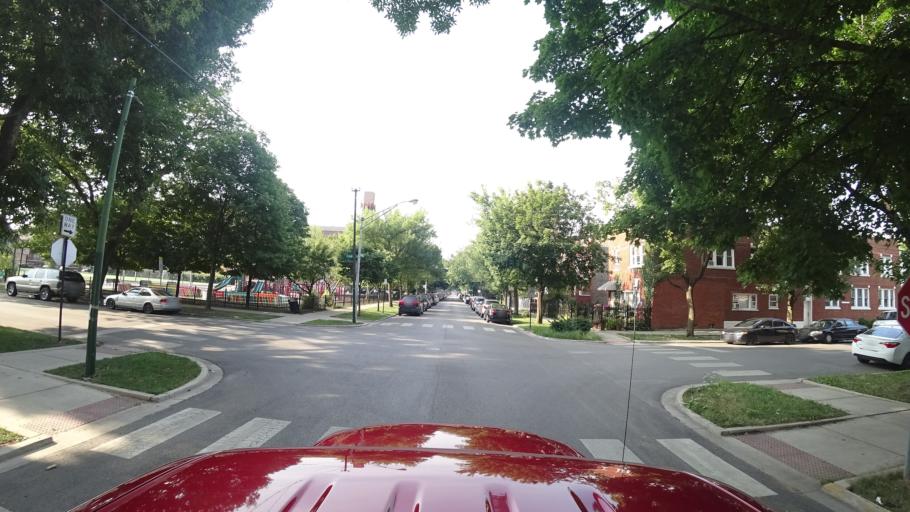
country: US
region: Illinois
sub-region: Cook County
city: Chicago
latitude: 41.8137
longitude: -87.7005
